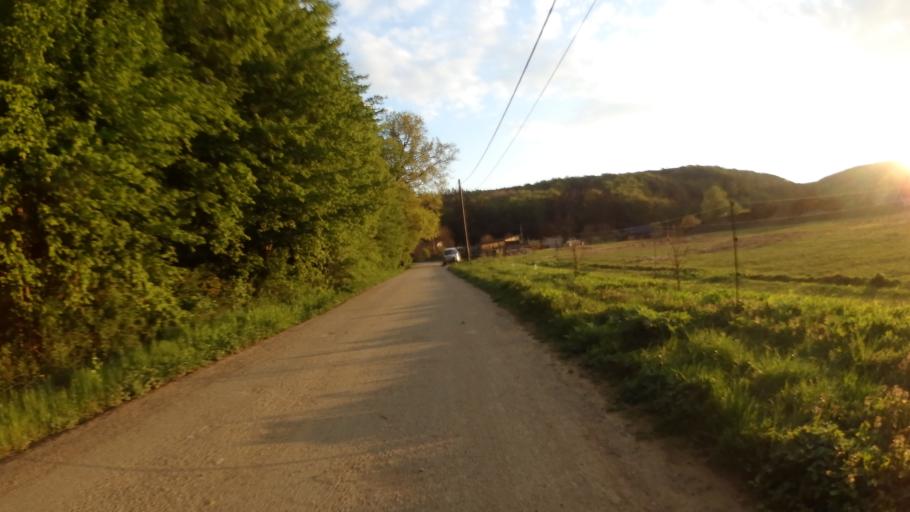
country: CZ
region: South Moravian
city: Strelice
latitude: 49.1379
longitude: 16.4765
